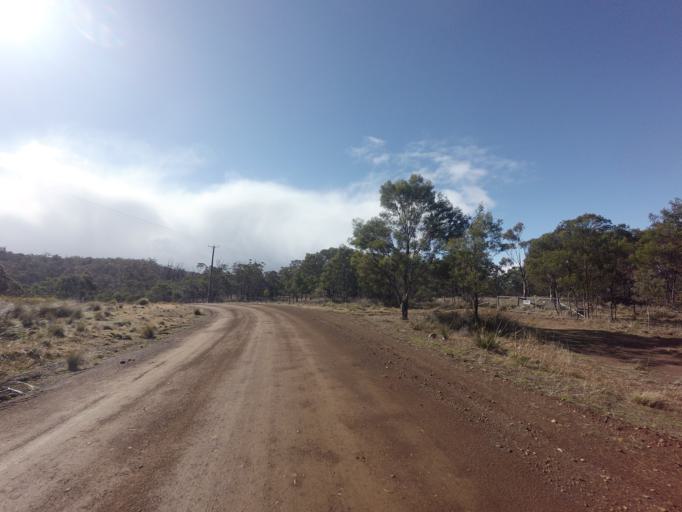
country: AU
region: Tasmania
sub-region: Sorell
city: Sorell
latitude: -42.4083
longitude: 147.9550
